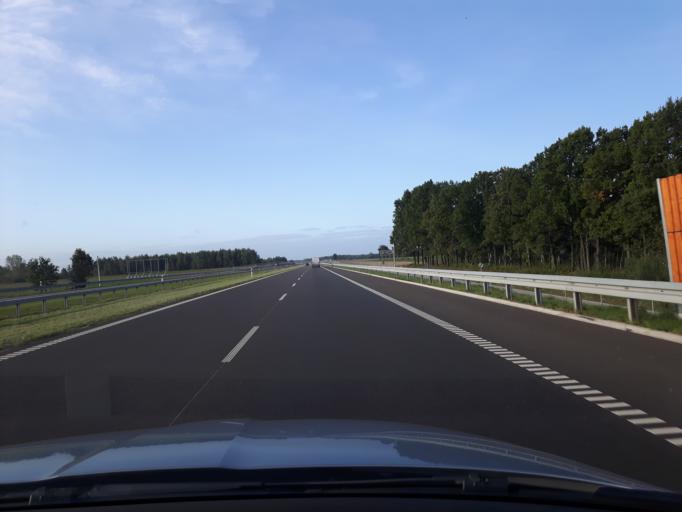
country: PL
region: Masovian Voivodeship
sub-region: Powiat radomski
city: Zakrzew
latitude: 51.4643
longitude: 21.0471
